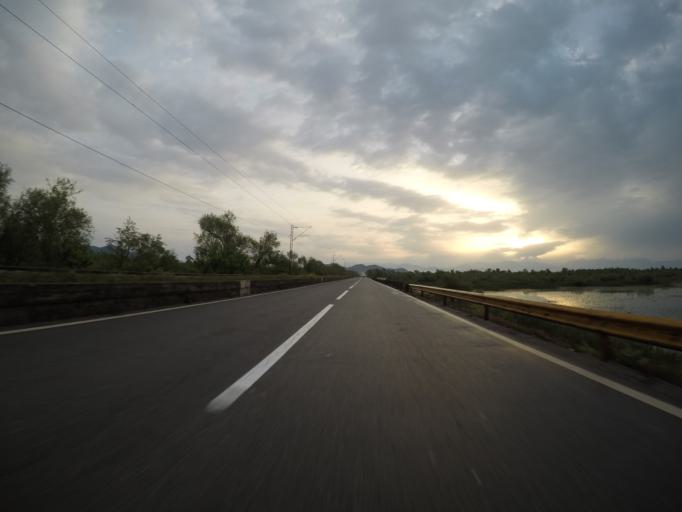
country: ME
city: Mojanovici
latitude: 42.2855
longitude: 19.1441
